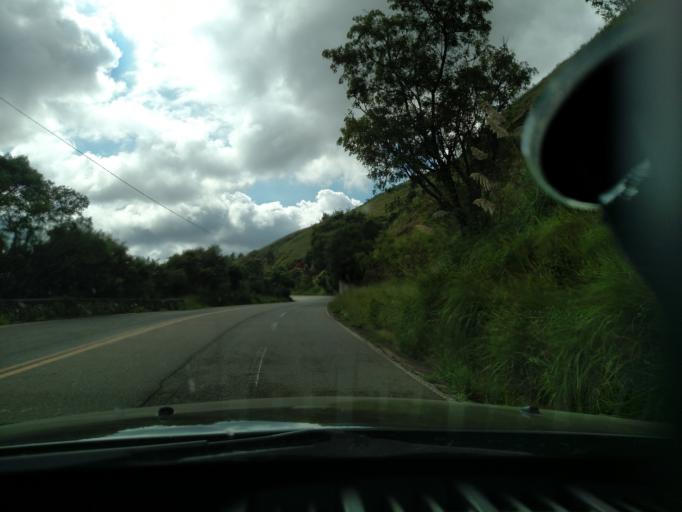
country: BR
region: Santa Catarina
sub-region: Lages
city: Lages
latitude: -27.8666
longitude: -50.1925
